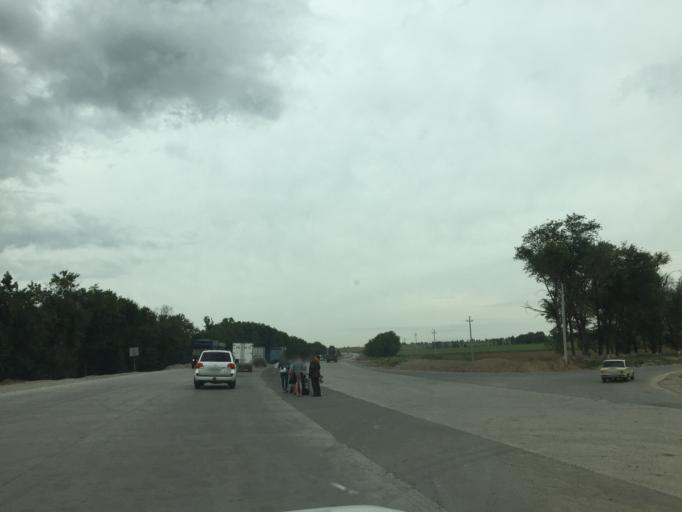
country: KZ
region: Ongtustik Qazaqstan
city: Sastobe
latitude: 42.5025
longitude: 69.9617
